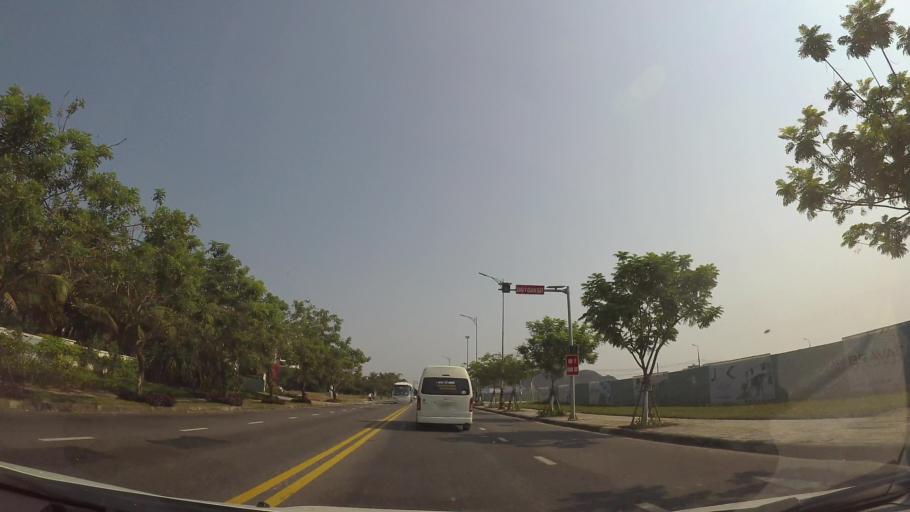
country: VN
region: Da Nang
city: Ngu Hanh Son
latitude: 16.0160
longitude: 108.2607
